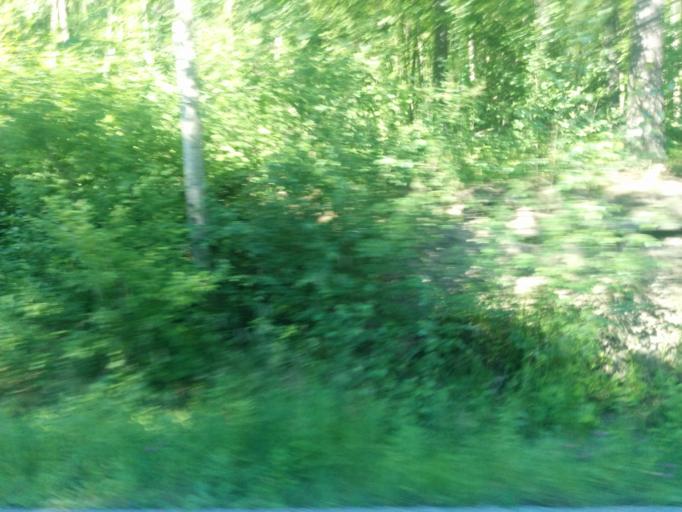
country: FI
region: Pirkanmaa
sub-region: Tampere
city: Tampere
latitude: 61.5016
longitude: 23.8543
